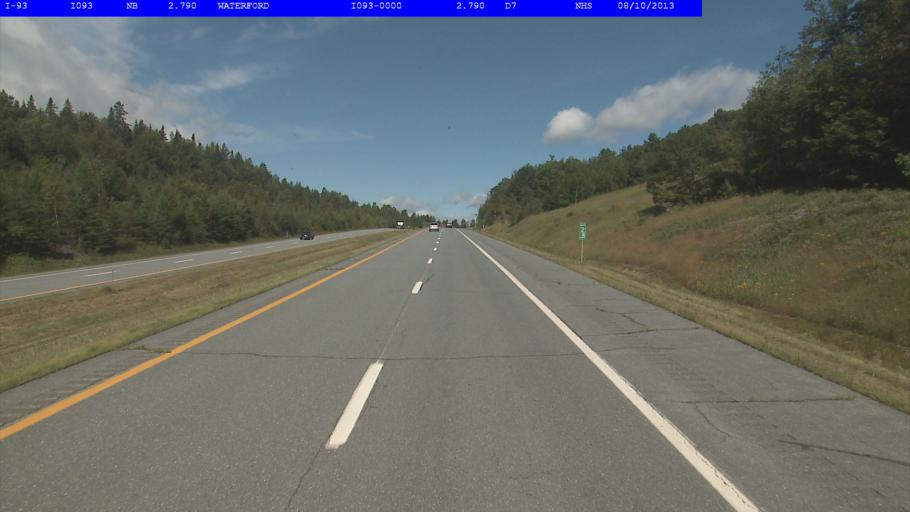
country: US
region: Vermont
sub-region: Caledonia County
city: Saint Johnsbury
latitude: 44.3782
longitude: -71.9158
